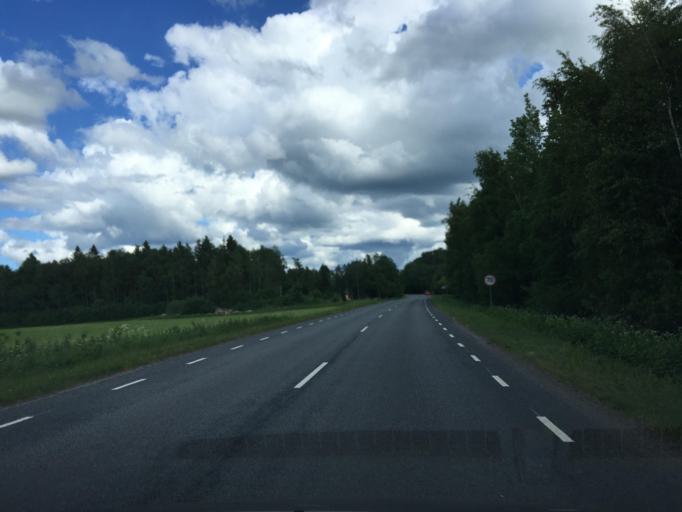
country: EE
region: Paernumaa
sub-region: Halinga vald
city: Parnu-Jaagupi
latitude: 58.6121
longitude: 24.4844
